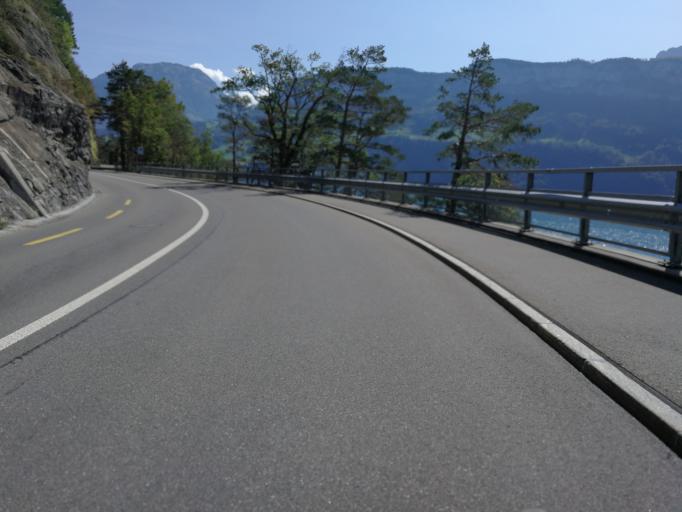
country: CH
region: Schwyz
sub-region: Bezirk Gersau
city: Gersau
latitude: 46.9885
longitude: 8.5343
